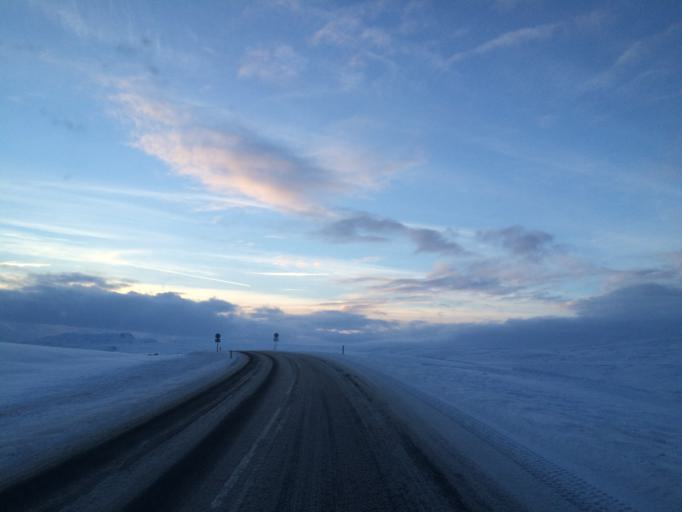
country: IS
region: South
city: Hveragerdi
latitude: 64.2382
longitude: -21.1897
